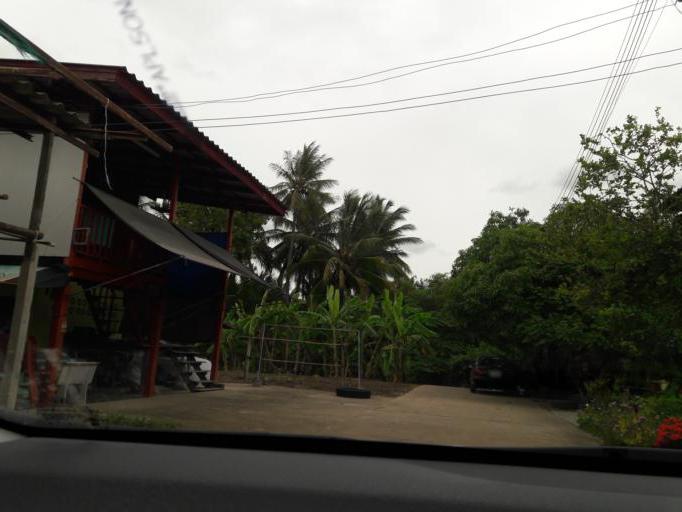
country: TH
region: Ratchaburi
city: Damnoen Saduak
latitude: 13.5498
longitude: 100.0315
